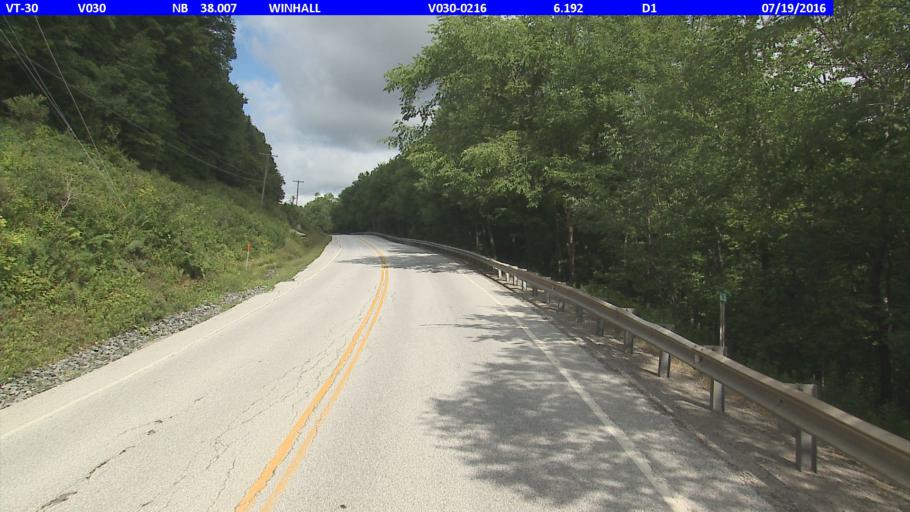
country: US
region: Vermont
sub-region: Bennington County
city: Manchester Center
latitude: 43.1919
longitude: -72.9455
